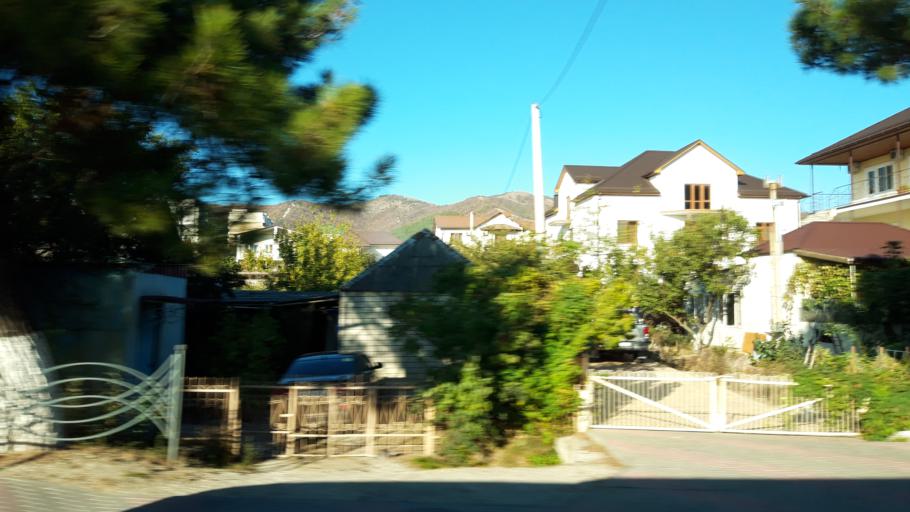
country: RU
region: Krasnodarskiy
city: Kabardinka
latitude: 44.6498
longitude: 37.9451
